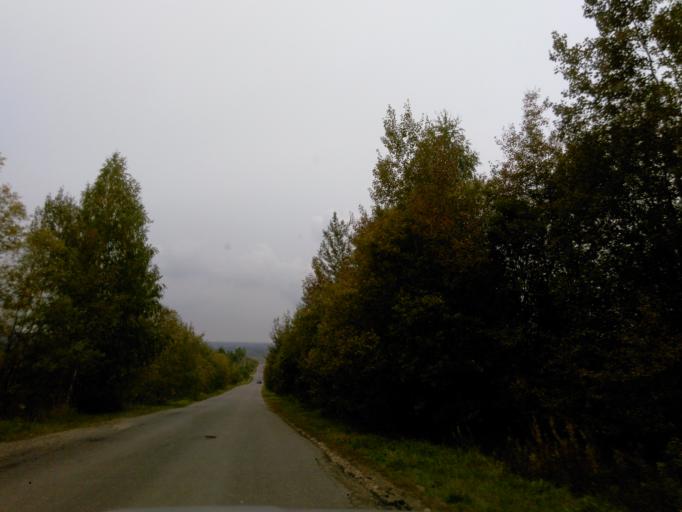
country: RU
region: Moskovskaya
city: Mendeleyevo
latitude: 56.1058
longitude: 37.2570
